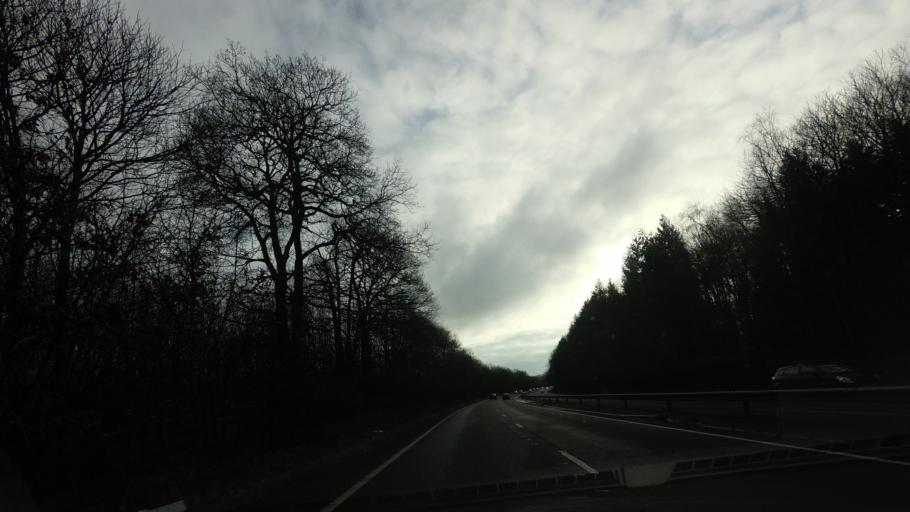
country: GB
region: England
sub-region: Kent
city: Sevenoaks
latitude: 51.2658
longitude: 0.1697
